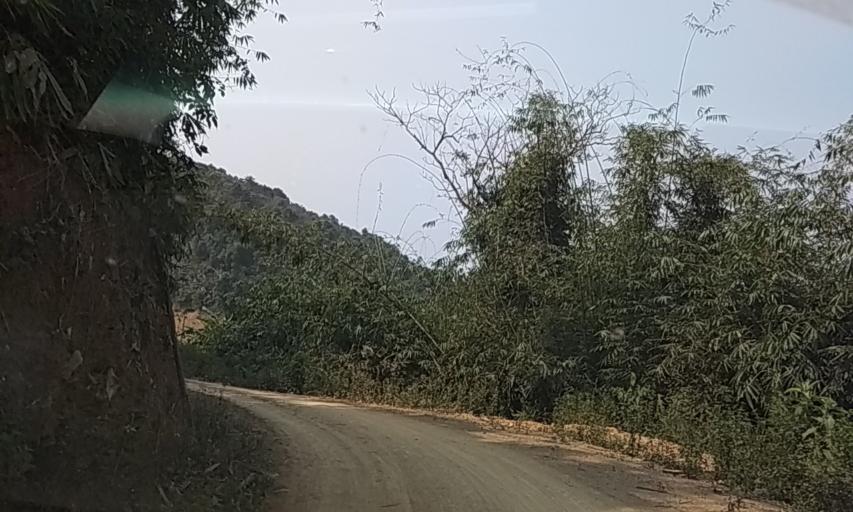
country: LA
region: Phongsali
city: Phongsali
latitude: 21.4651
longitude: 102.4248
